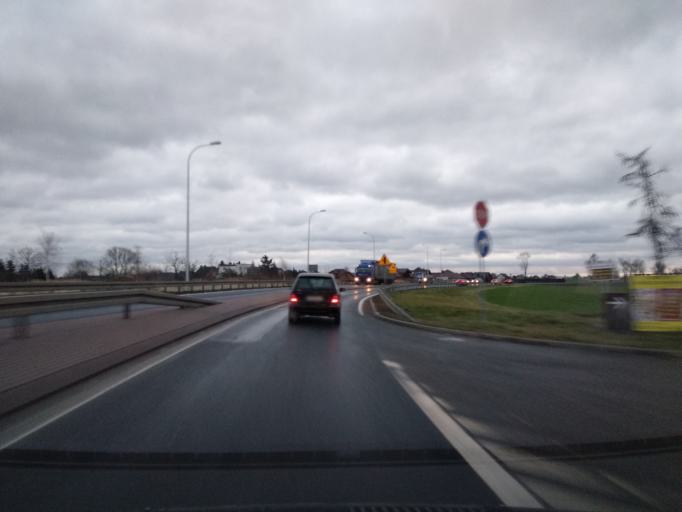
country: PL
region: Greater Poland Voivodeship
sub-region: Powiat koninski
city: Rychwal
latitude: 52.0669
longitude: 18.1631
